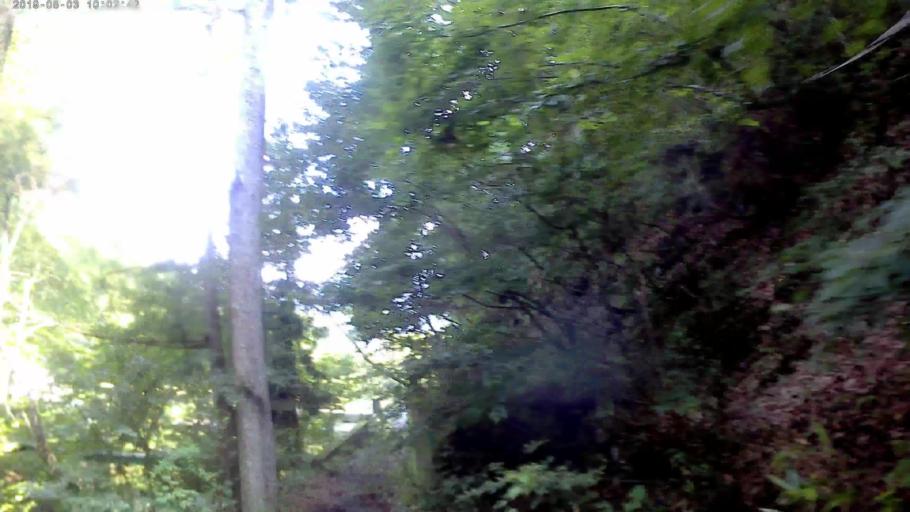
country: JP
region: Yamanashi
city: Enzan
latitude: 35.6339
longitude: 138.7688
